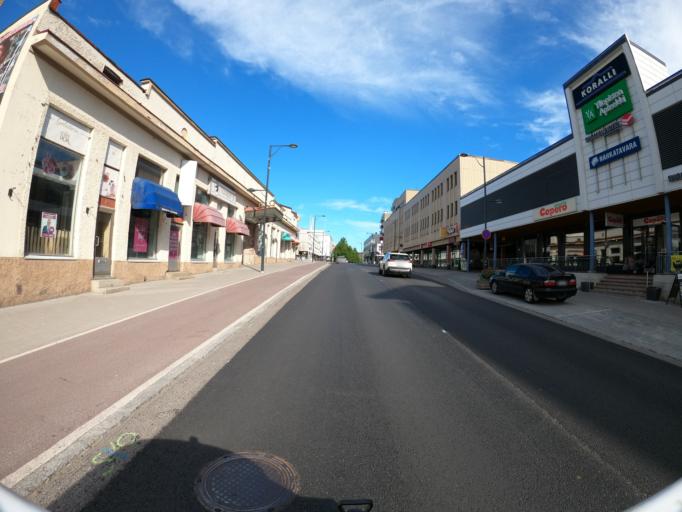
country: FI
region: Southern Savonia
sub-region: Savonlinna
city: Savonlinna
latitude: 61.8702
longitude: 28.8783
